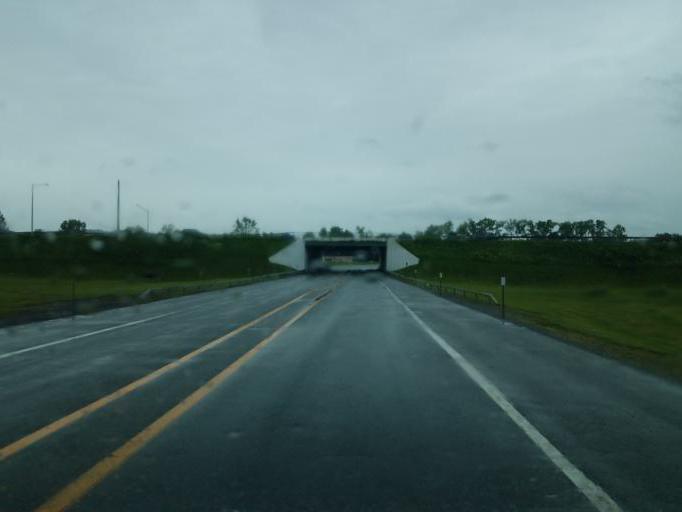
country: US
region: New York
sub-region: Herkimer County
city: Herkimer
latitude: 43.0169
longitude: -74.9896
